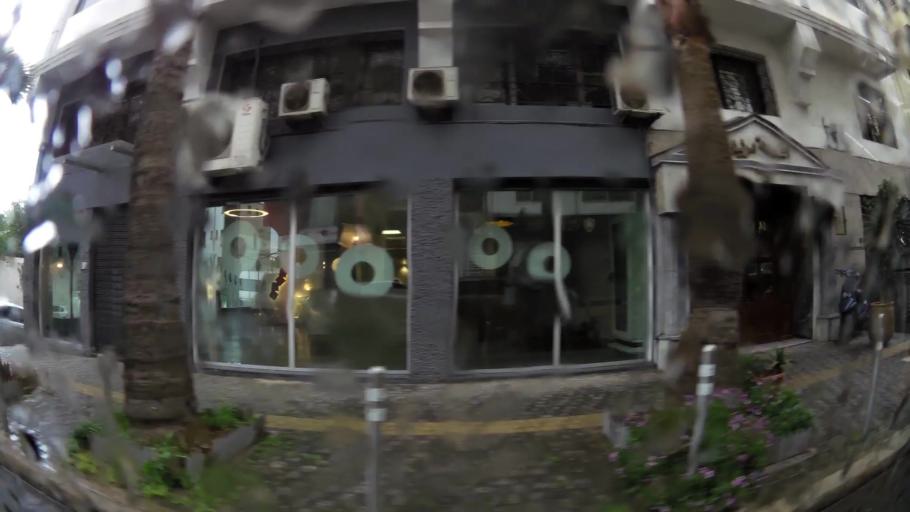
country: MA
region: Grand Casablanca
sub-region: Casablanca
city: Casablanca
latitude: 33.5804
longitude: -7.6174
